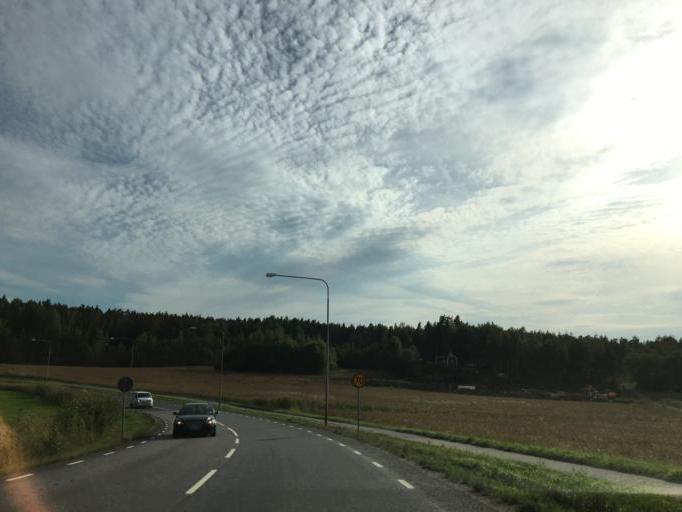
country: SE
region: Soedermanland
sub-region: Eskilstuna Kommun
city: Torshalla
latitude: 59.4304
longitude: 16.4539
